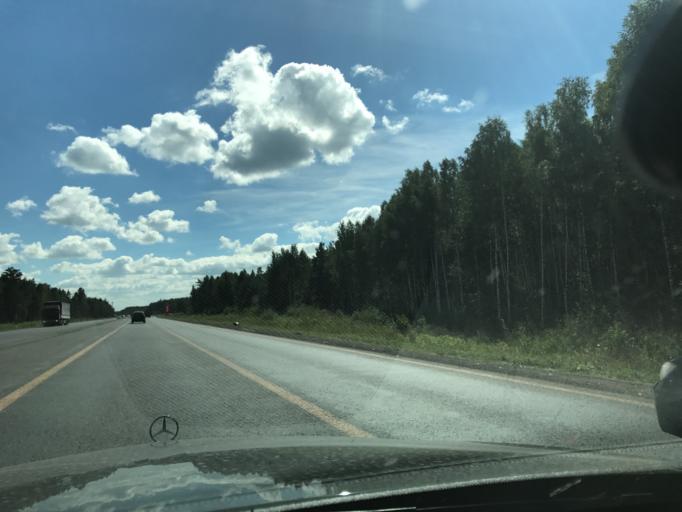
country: RU
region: Nizjnij Novgorod
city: Gorbatovka
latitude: 56.2791
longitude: 43.7007
